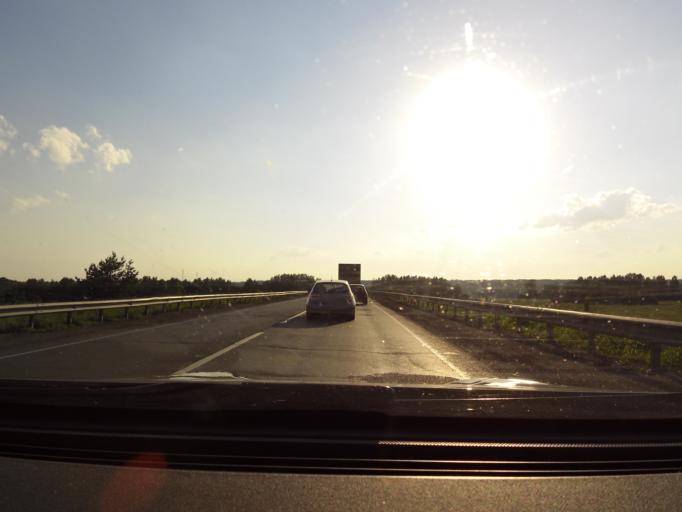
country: RU
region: Sverdlovsk
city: Druzhinino
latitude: 56.8111
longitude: 59.5212
